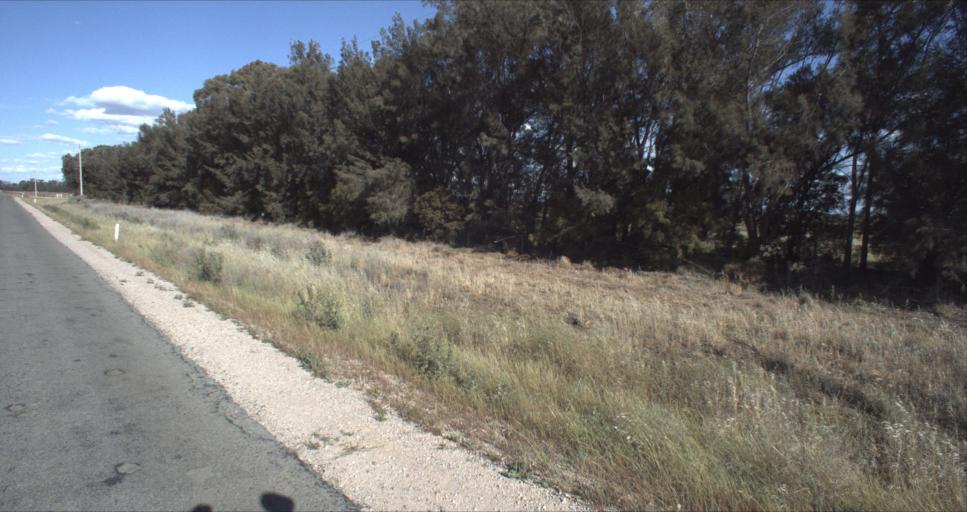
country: AU
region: New South Wales
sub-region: Leeton
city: Leeton
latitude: -34.4585
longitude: 146.2671
